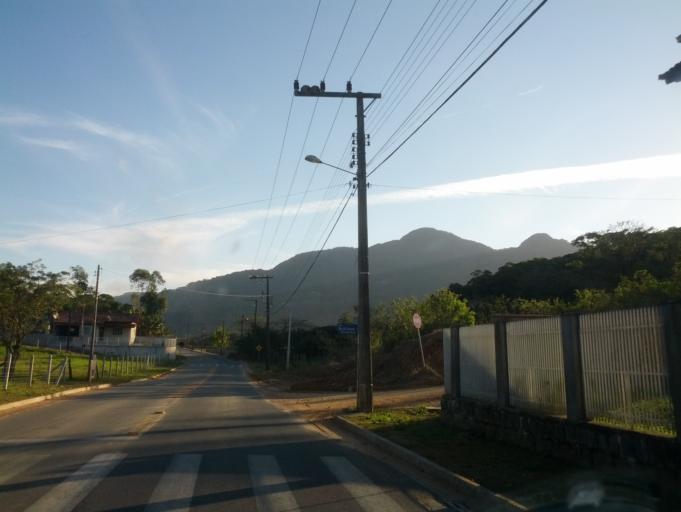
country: BR
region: Santa Catarina
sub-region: Indaial
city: Indaial
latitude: -26.9074
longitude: -49.2628
